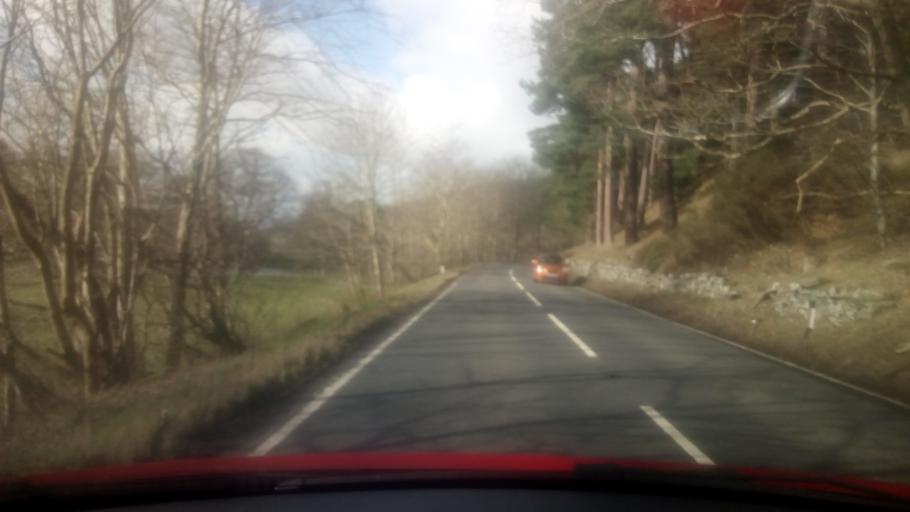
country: GB
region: Scotland
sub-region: The Scottish Borders
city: Innerleithen
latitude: 55.6279
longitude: -2.9775
